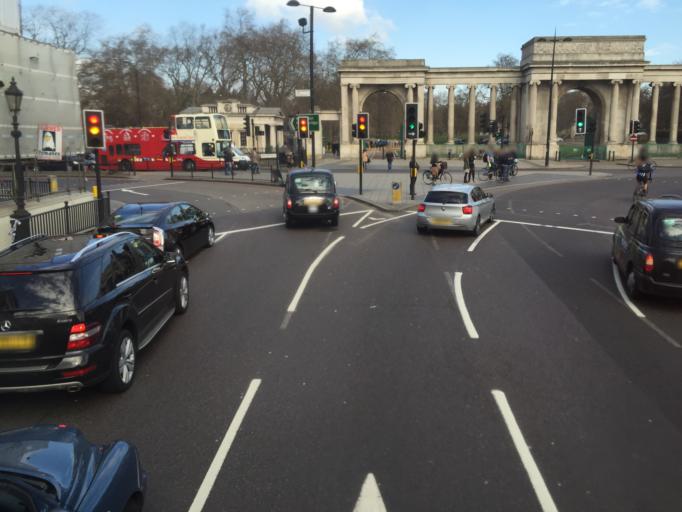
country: GB
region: England
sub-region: Greater London
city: Chelsea
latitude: 51.5027
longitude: -0.1523
